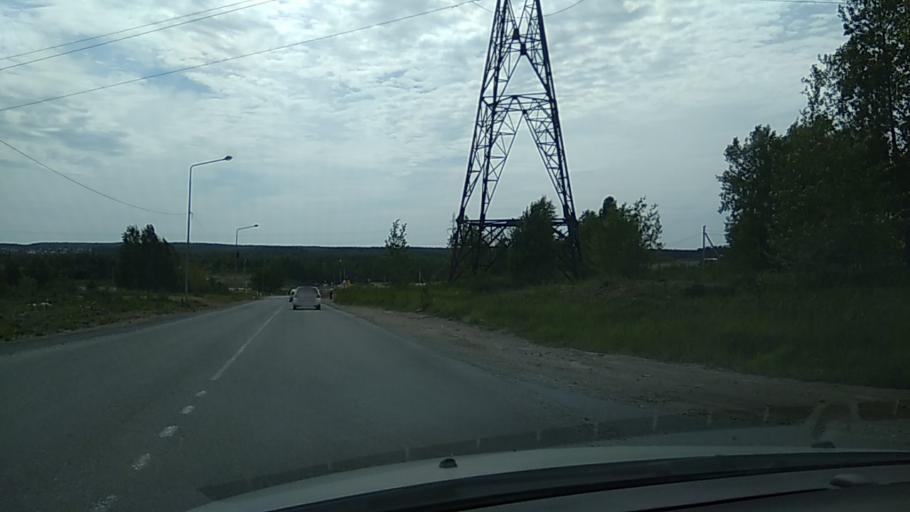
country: RU
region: Sverdlovsk
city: Verkhnyaya Pyshma
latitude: 56.9547
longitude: 60.5866
